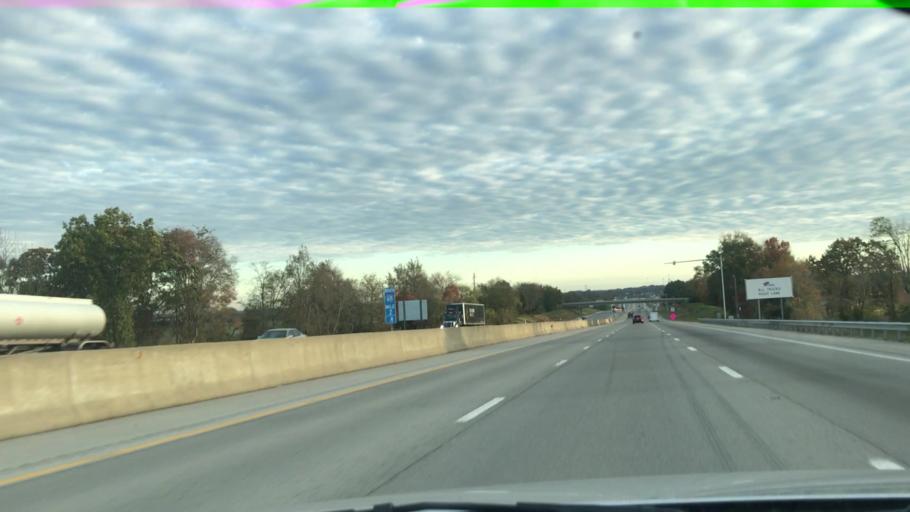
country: US
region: Kentucky
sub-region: Simpson County
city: Franklin
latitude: 36.6743
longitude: -86.5487
